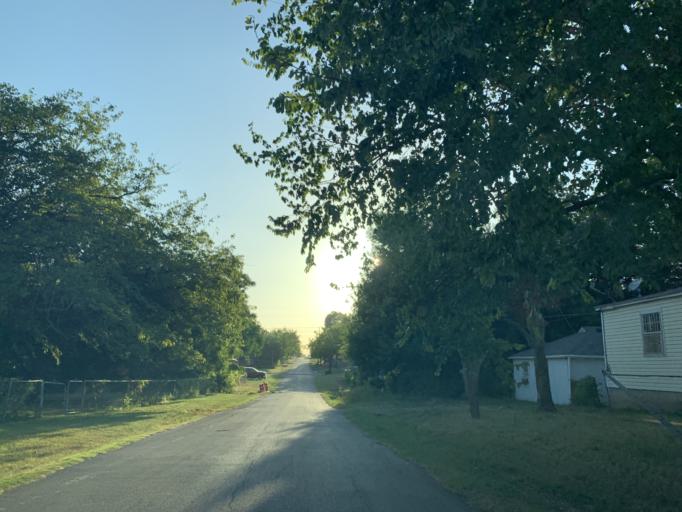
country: US
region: Texas
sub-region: Dallas County
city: Dallas
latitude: 32.7030
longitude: -96.8110
